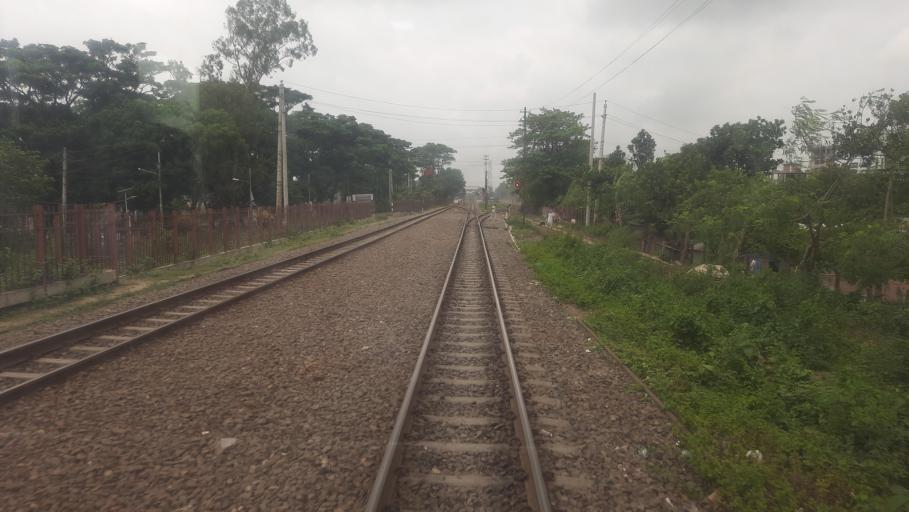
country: BD
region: Dhaka
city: Bhairab Bazar
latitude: 24.0504
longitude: 90.9821
